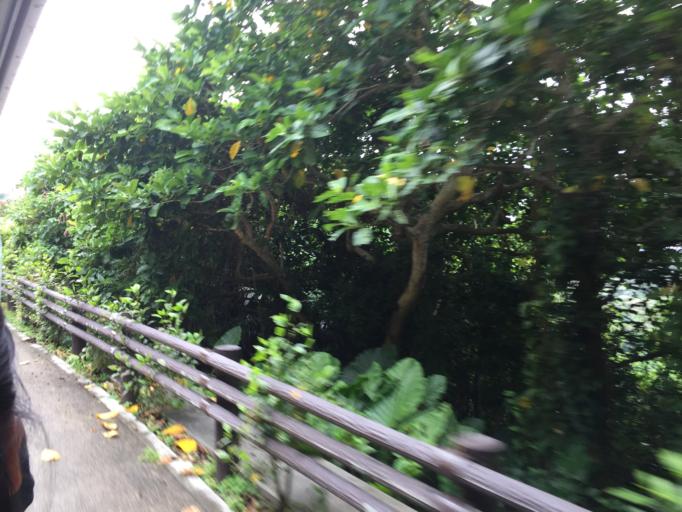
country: JP
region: Okinawa
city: Chatan
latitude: 26.2846
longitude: 127.8011
